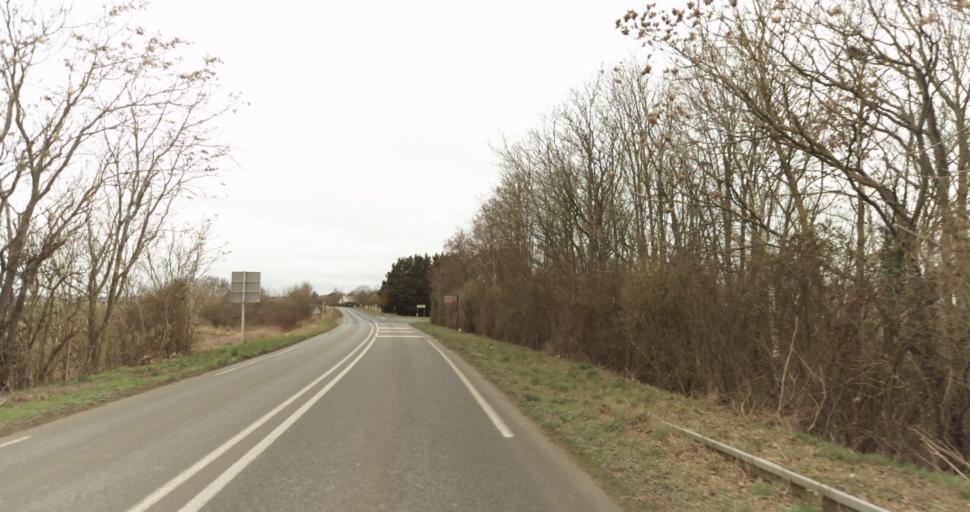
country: FR
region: Pays de la Loire
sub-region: Departement de Maine-et-Loire
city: Doue-la-Fontaine
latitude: 47.1823
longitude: -0.2639
